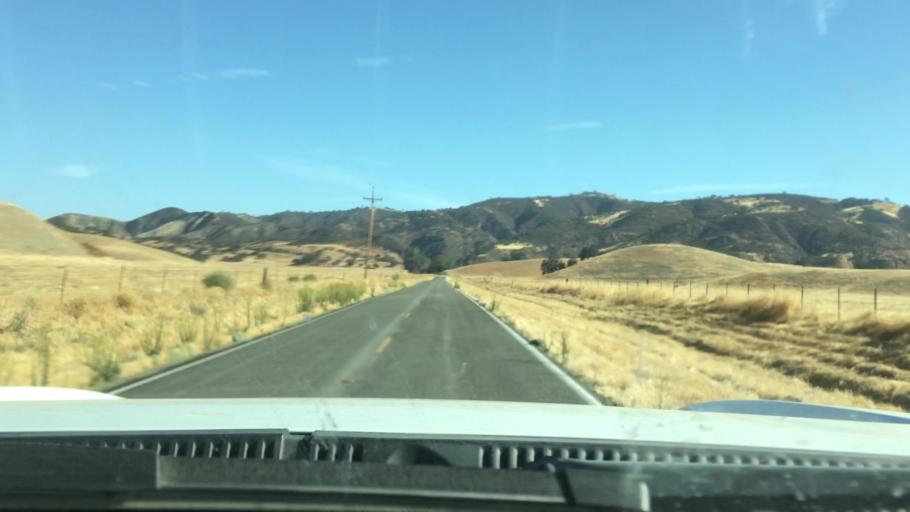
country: US
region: California
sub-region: Monterey County
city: King City
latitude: 36.3955
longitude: -120.9998
